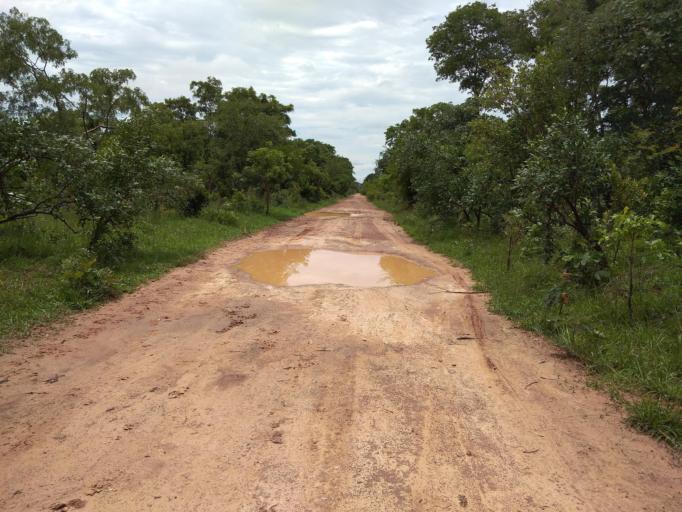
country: ZM
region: Central
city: Kapiri Mposhi
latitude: -13.5260
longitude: 28.8847
